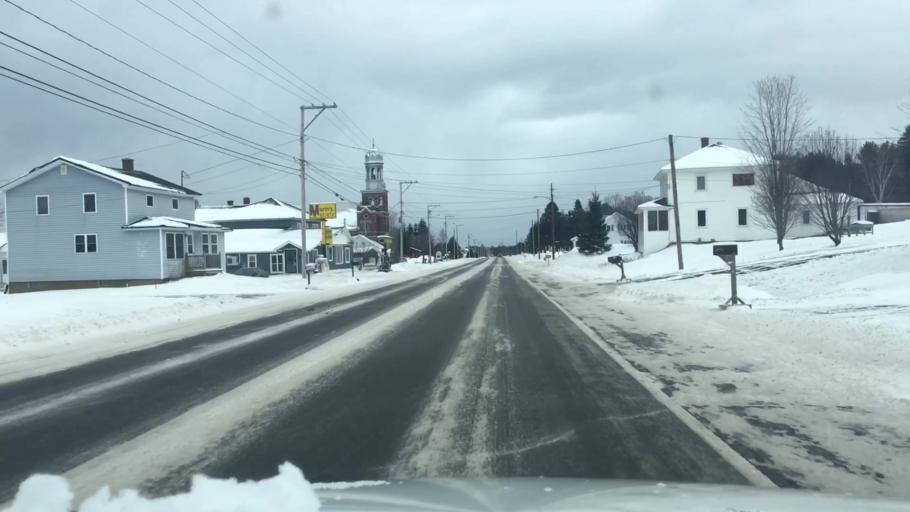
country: US
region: Maine
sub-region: Aroostook County
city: Madawaska
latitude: 47.3494
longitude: -68.2804
